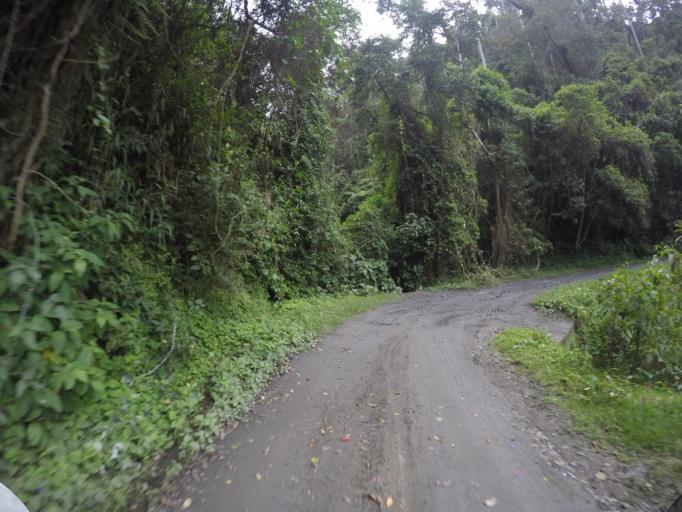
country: CO
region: Tolima
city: Cajamarca
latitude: 4.5384
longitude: -75.4432
